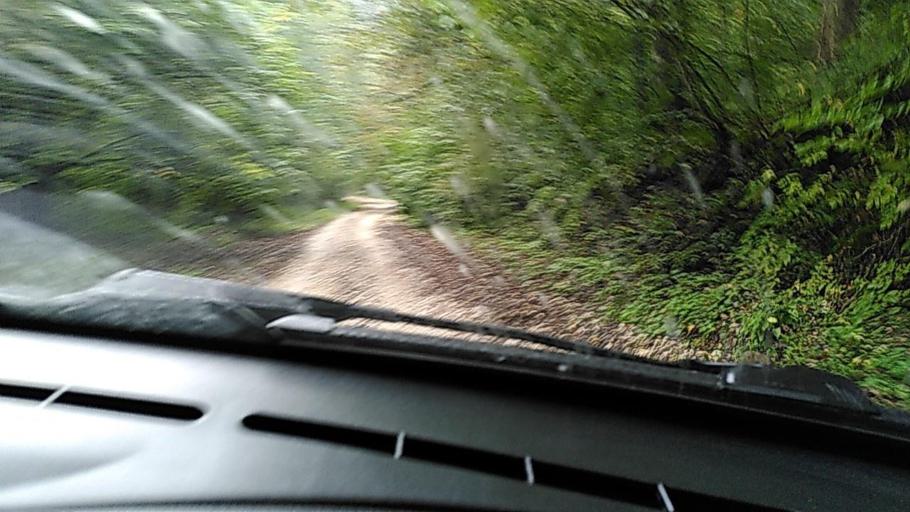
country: RU
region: Kabardino-Balkariya
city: Belaya Rechka
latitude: 43.3958
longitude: 43.4491
